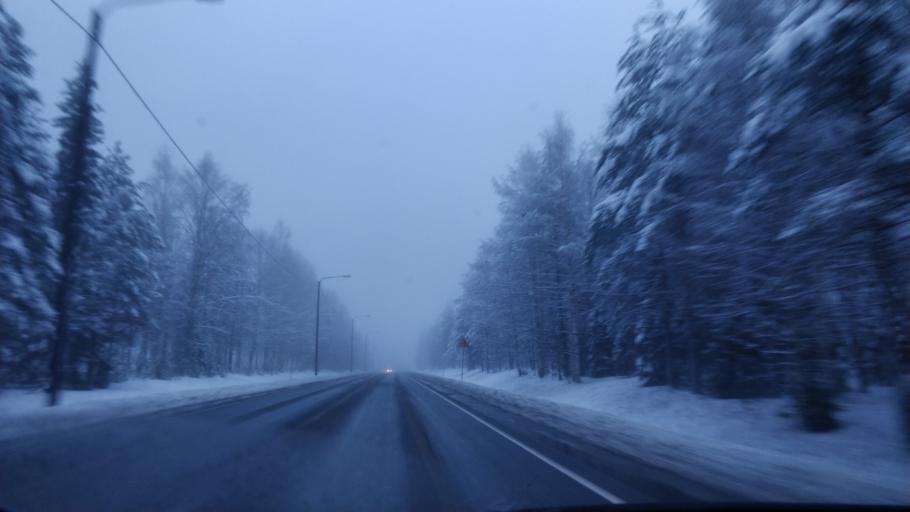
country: FI
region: Lapland
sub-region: Kemi-Tornio
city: Tervola
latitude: 66.1331
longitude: 24.9094
